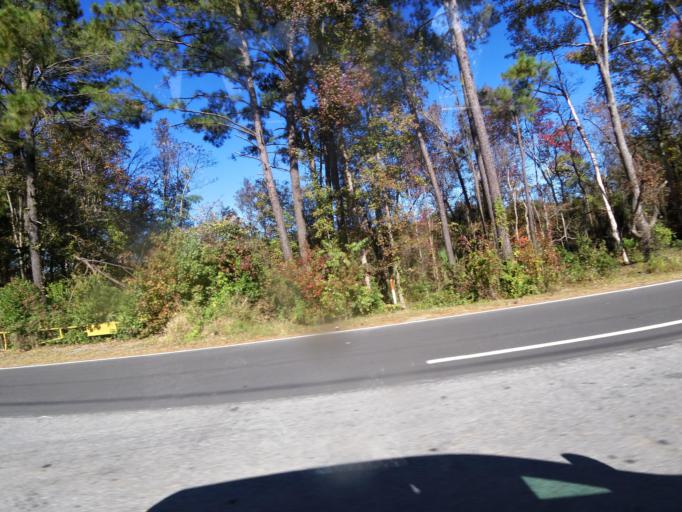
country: US
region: Georgia
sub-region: Chatham County
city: Savannah
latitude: 32.0775
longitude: -81.1290
